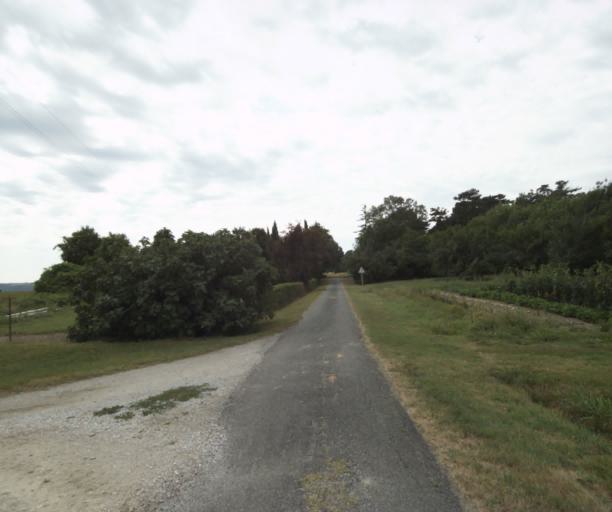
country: FR
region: Midi-Pyrenees
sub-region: Departement de la Haute-Garonne
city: Saint-Felix-Lauragais
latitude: 43.4313
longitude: 1.9262
